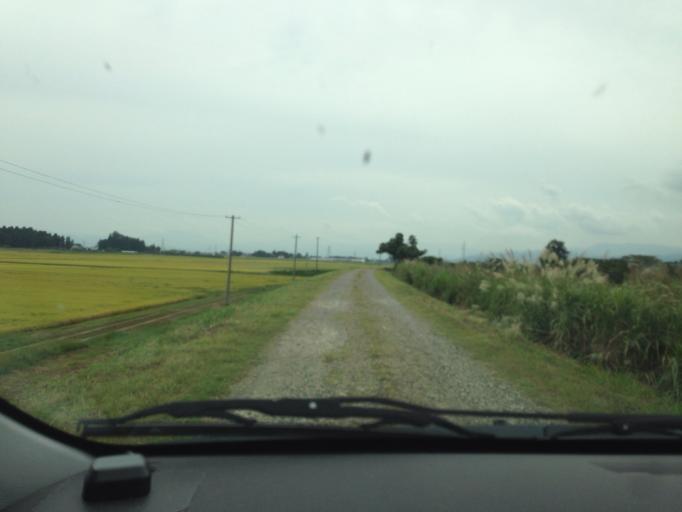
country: JP
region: Fukushima
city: Kitakata
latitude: 37.6006
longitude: 139.8228
